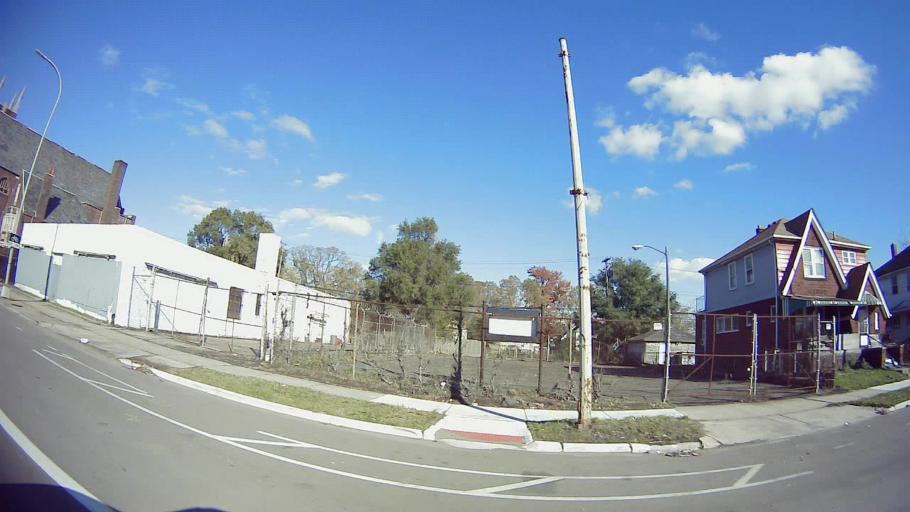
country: US
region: Michigan
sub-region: Wayne County
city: Dearborn
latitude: 42.3330
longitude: -83.1208
